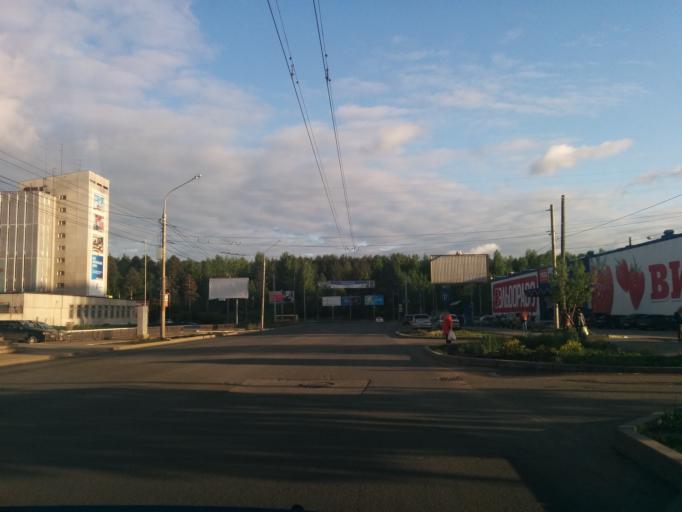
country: RU
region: Perm
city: Kondratovo
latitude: 57.9973
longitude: 56.1669
